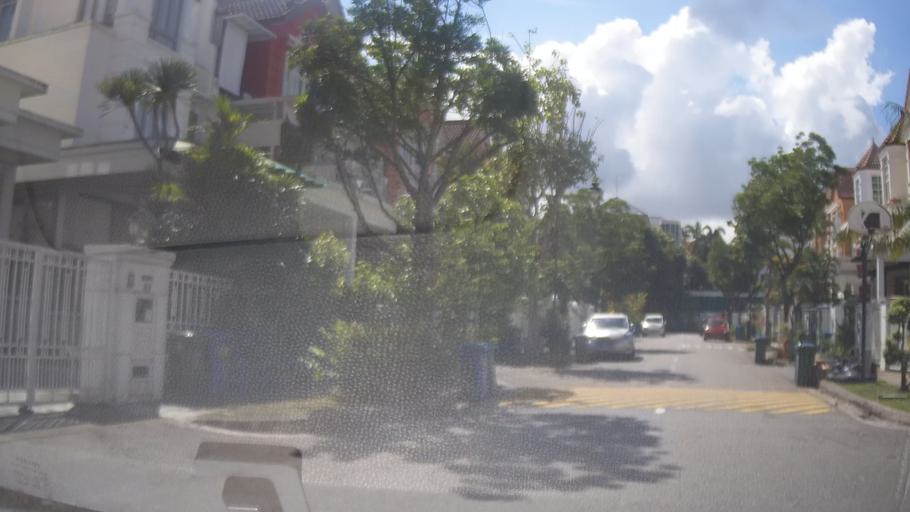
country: MY
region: Johor
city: Johor Bahru
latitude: 1.4274
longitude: 103.7765
